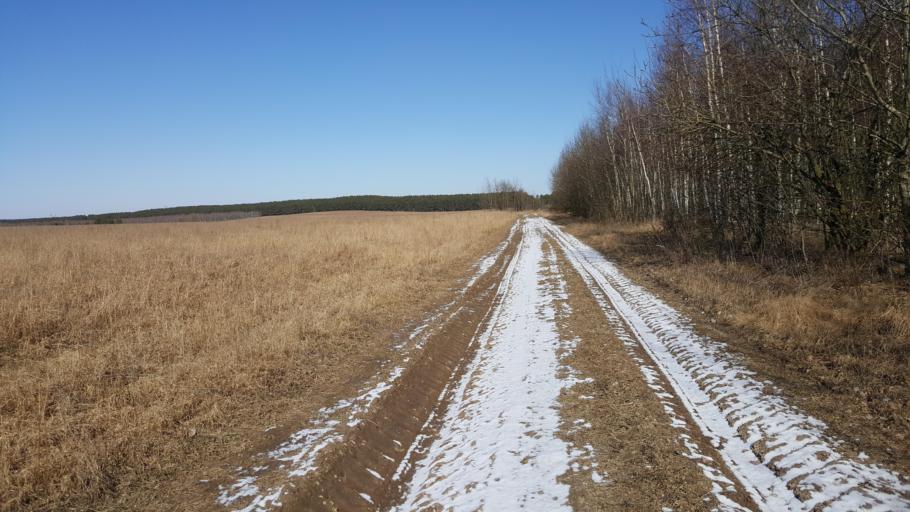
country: BY
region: Brest
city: Kamyanyets
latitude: 52.3712
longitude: 23.8342
